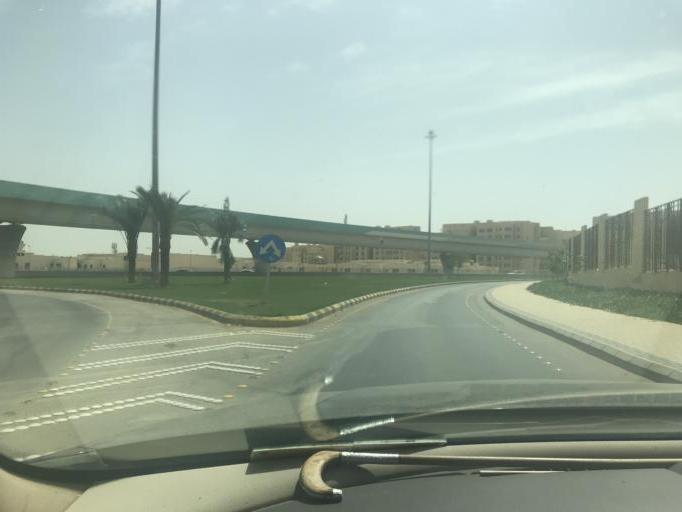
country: SA
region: Ar Riyad
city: Riyadh
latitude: 24.8204
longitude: 46.6993
